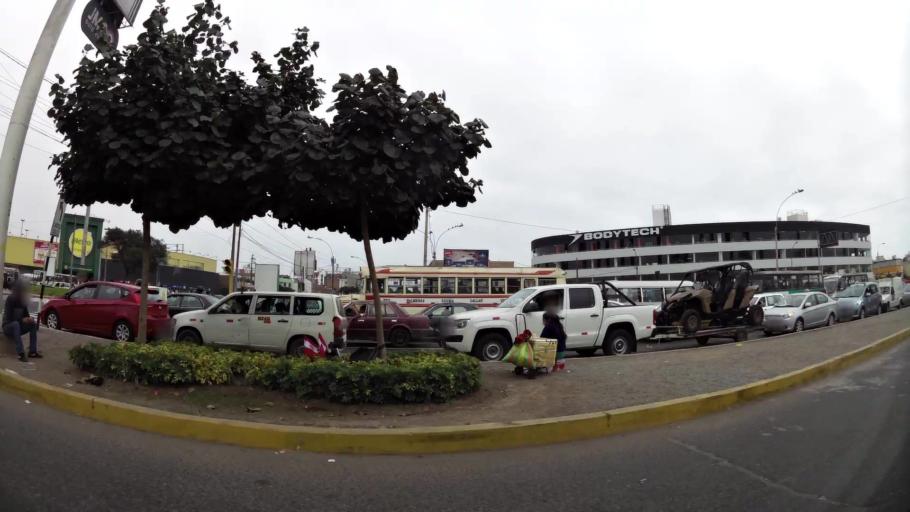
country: PE
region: Callao
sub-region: Callao
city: Callao
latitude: -12.0625
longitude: -77.0974
